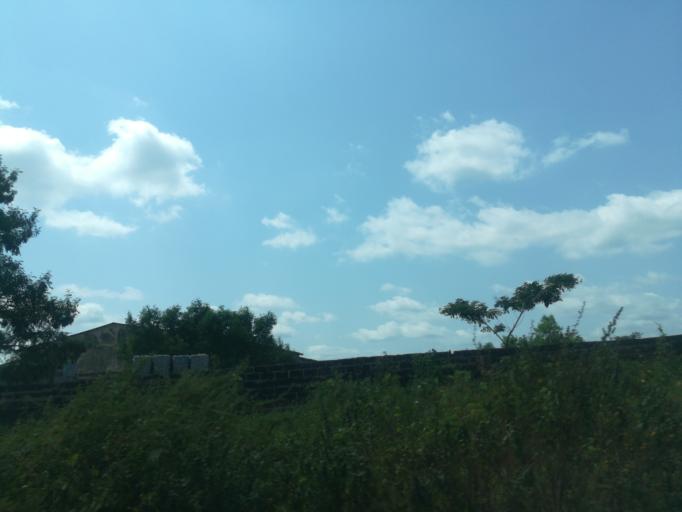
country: NG
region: Oyo
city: Moniya
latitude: 7.5616
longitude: 3.9096
